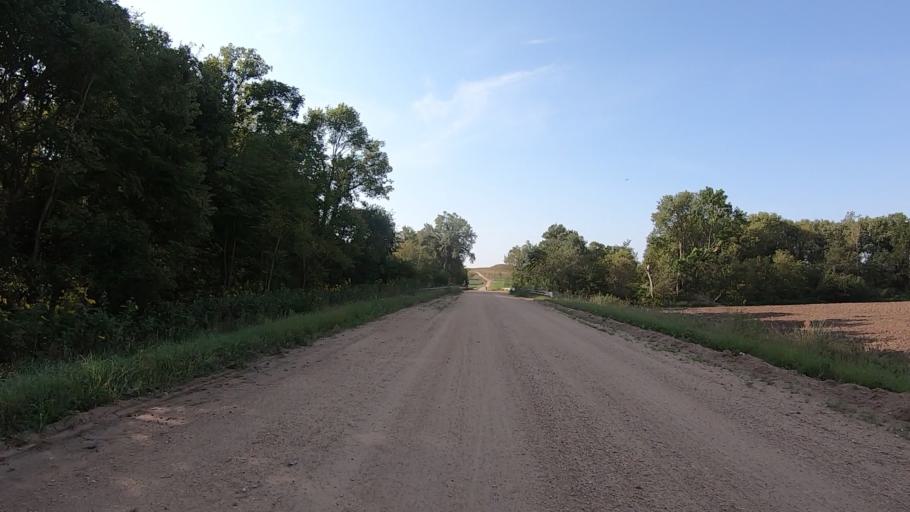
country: US
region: Kansas
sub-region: Marshall County
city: Blue Rapids
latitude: 39.6561
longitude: -96.8815
